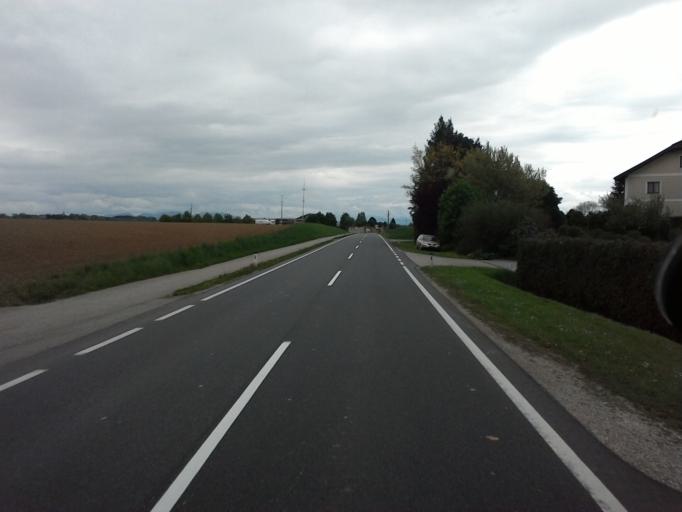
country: AT
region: Upper Austria
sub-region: Wels-Land
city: Sattledt
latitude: 48.0575
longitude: 14.0531
